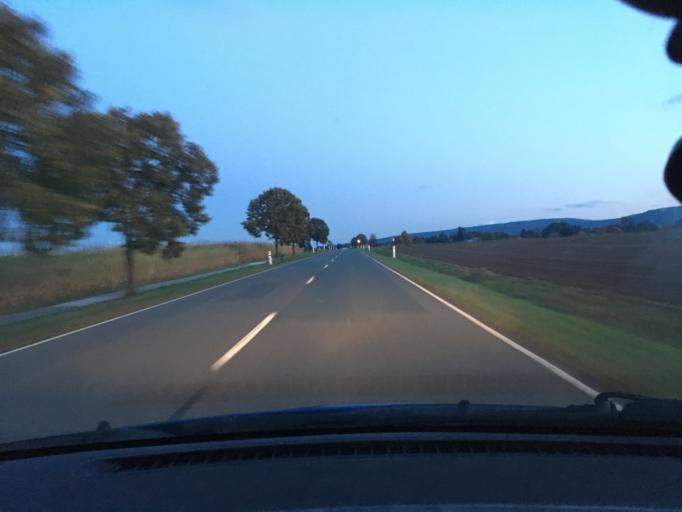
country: DE
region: Lower Saxony
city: Hulsede
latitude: 52.2493
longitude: 9.3728
